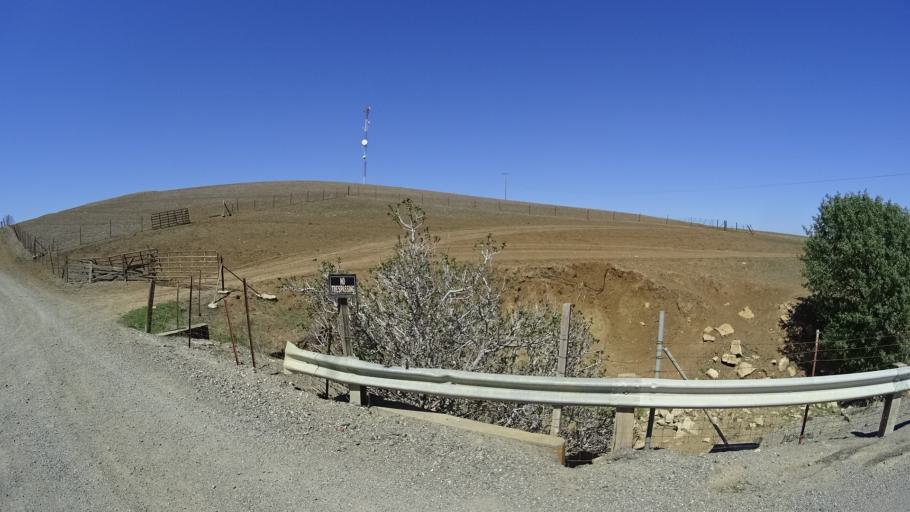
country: US
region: California
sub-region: Glenn County
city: Willows
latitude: 39.3997
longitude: -122.2902
